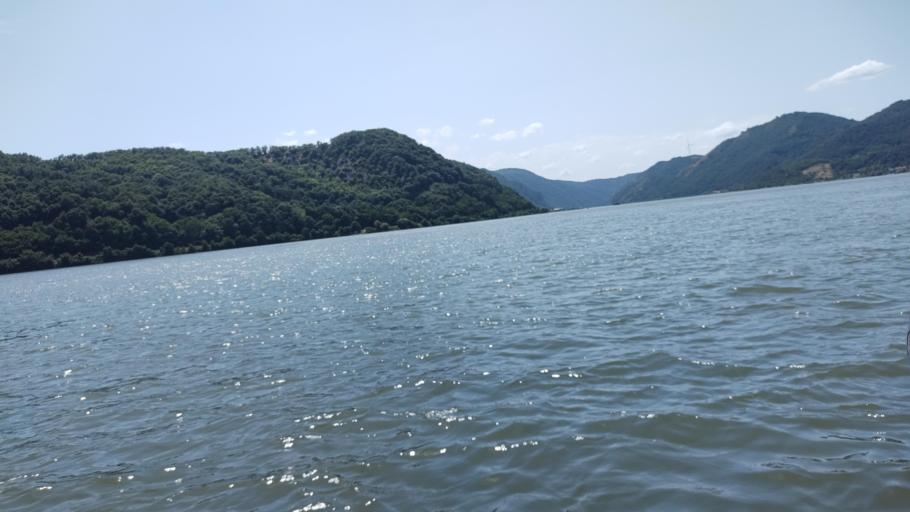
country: RS
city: Radenka
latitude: 44.6599
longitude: 21.7856
